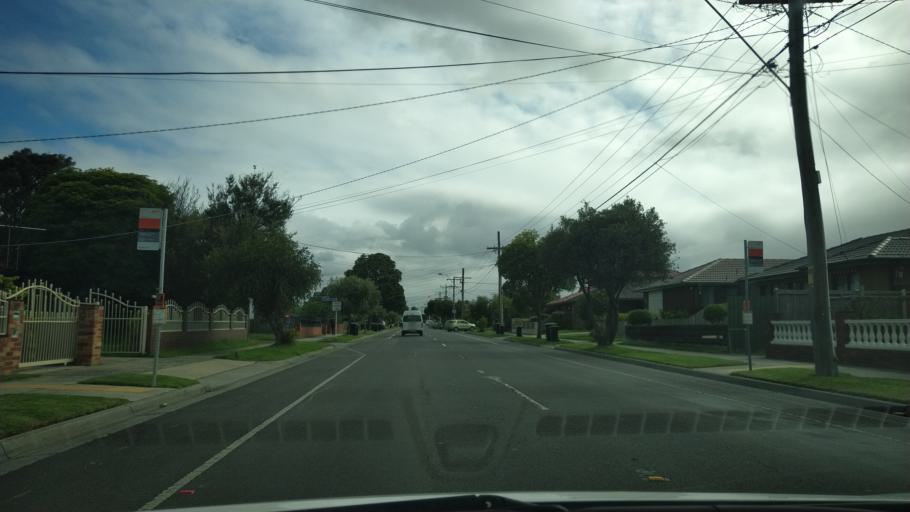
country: AU
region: Victoria
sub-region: Greater Dandenong
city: Keysborough
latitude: -37.9908
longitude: 145.1753
